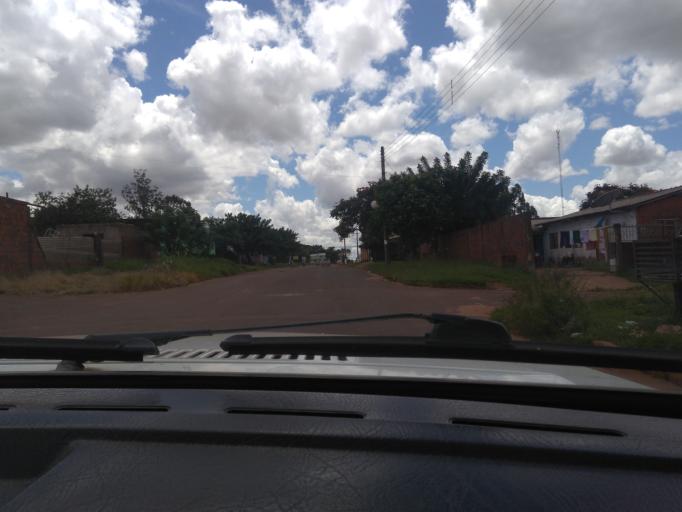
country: BR
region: Mato Grosso do Sul
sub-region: Ponta Pora
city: Ponta Pora
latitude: -22.5077
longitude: -55.7278
